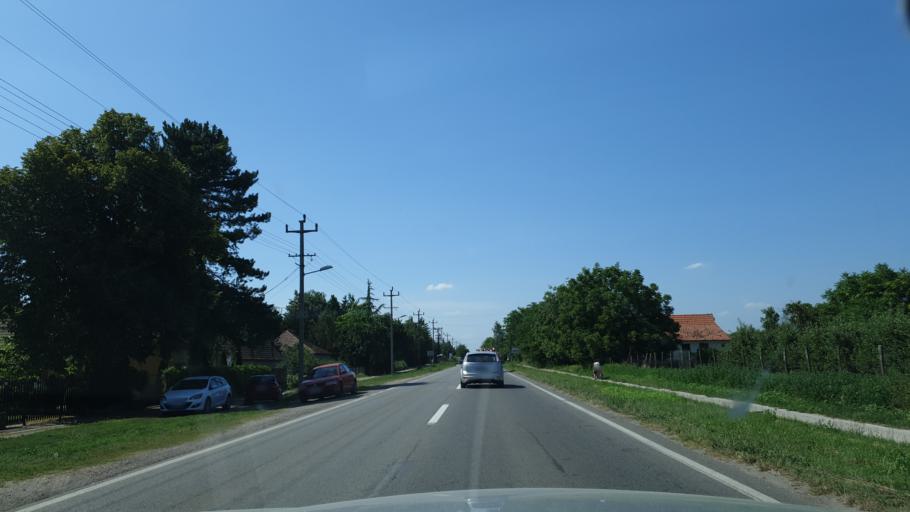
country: HU
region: Bacs-Kiskun
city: Kelebia
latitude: 46.1415
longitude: 19.5896
